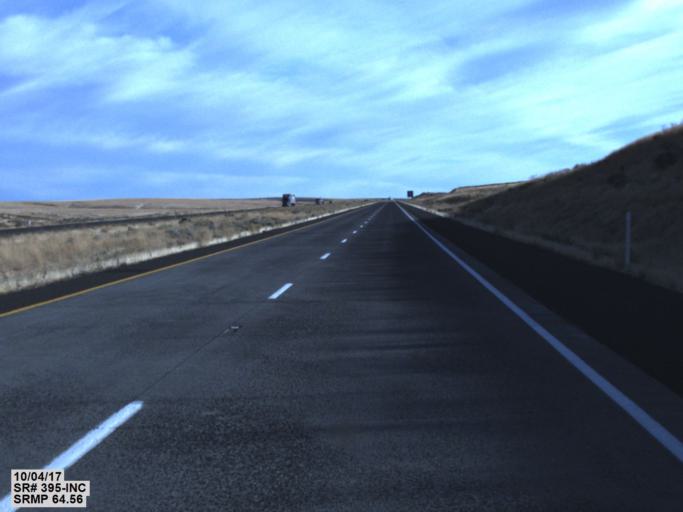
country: US
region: Washington
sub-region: Franklin County
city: Connell
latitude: 46.7730
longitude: -118.7759
